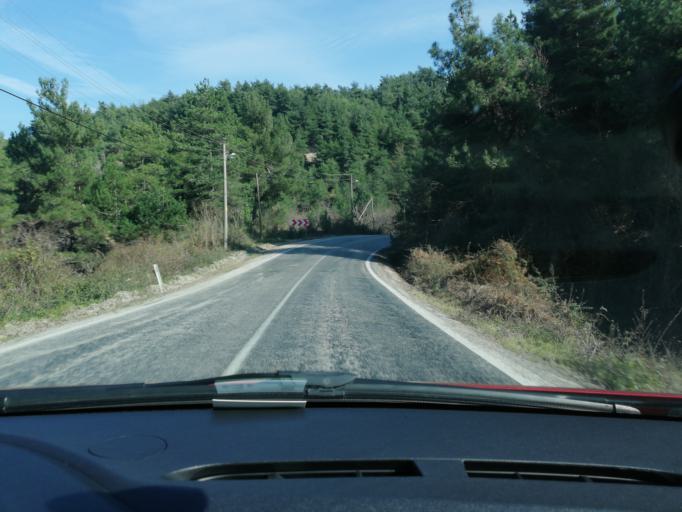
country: TR
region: Bartin
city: Kurucasile
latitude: 41.8362
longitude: 32.7075
